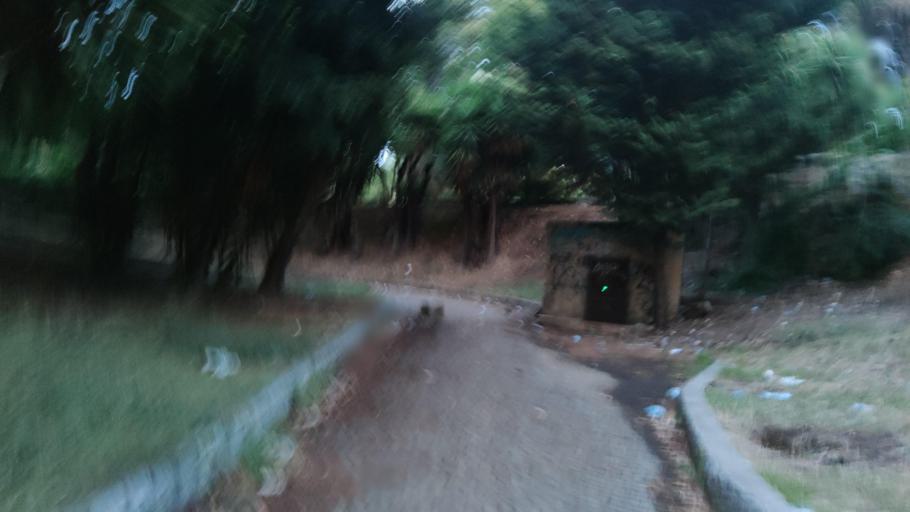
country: IT
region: Sicily
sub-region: Palermo
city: Palermo
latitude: 38.1321
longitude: 13.3513
